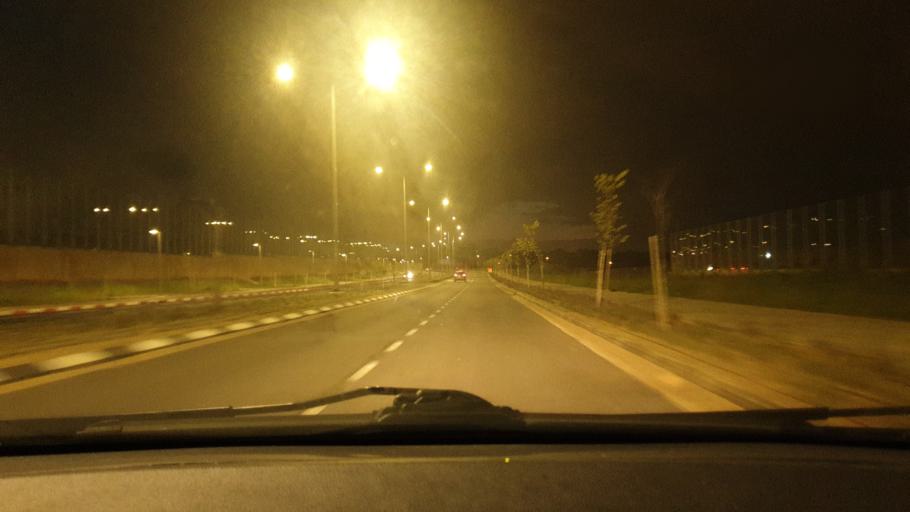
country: IL
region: Central District
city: Ramla
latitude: 31.9337
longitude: 34.8496
